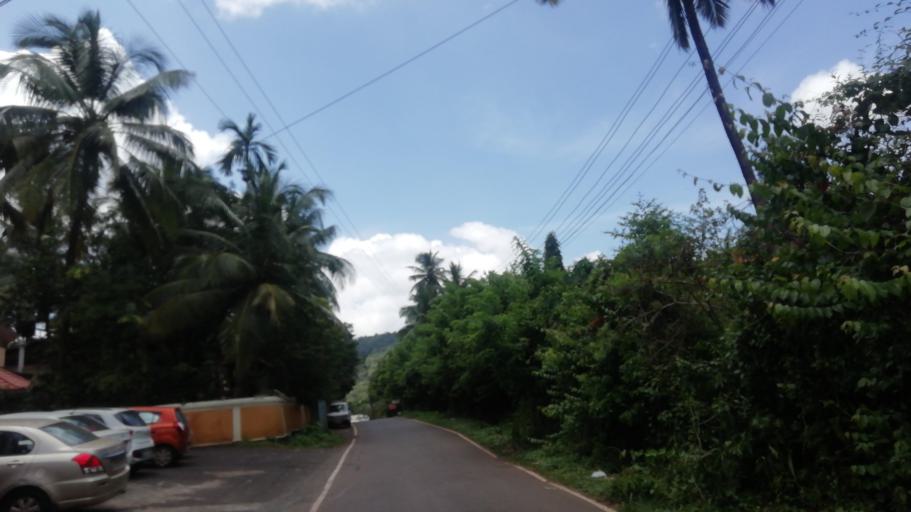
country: IN
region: Goa
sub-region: North Goa
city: Queula
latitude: 15.3861
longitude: 74.0030
